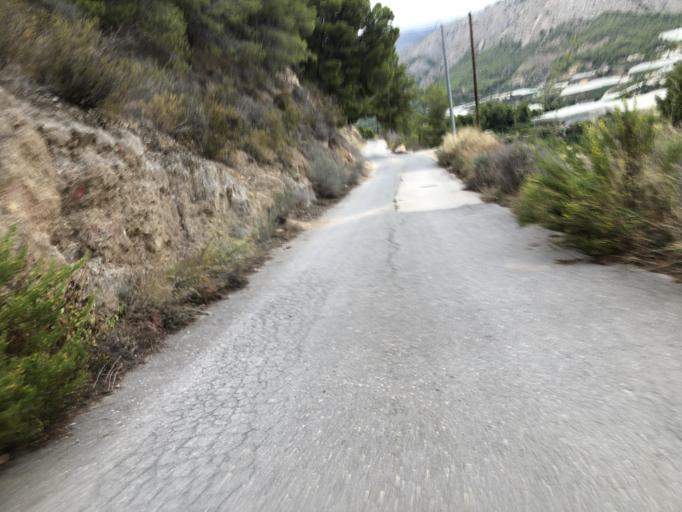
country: ES
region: Valencia
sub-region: Provincia de Alicante
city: Polop
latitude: 38.6363
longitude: -0.1323
